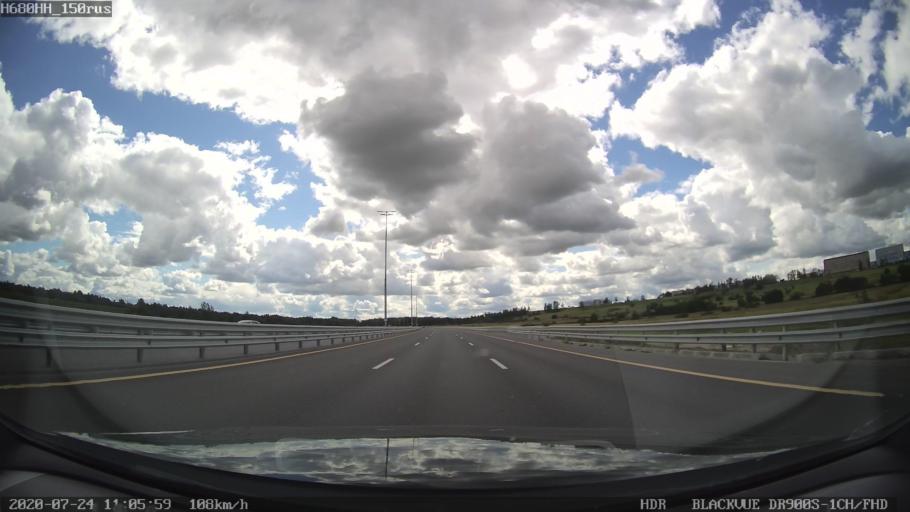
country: RU
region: St.-Petersburg
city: Shushary
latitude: 59.7695
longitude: 30.3652
